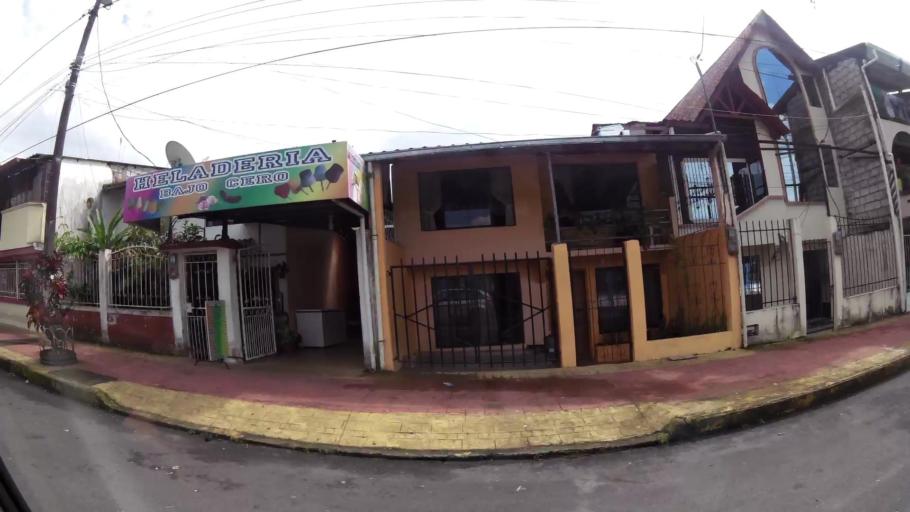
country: EC
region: Pastaza
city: Puyo
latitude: -1.4834
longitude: -78.0104
